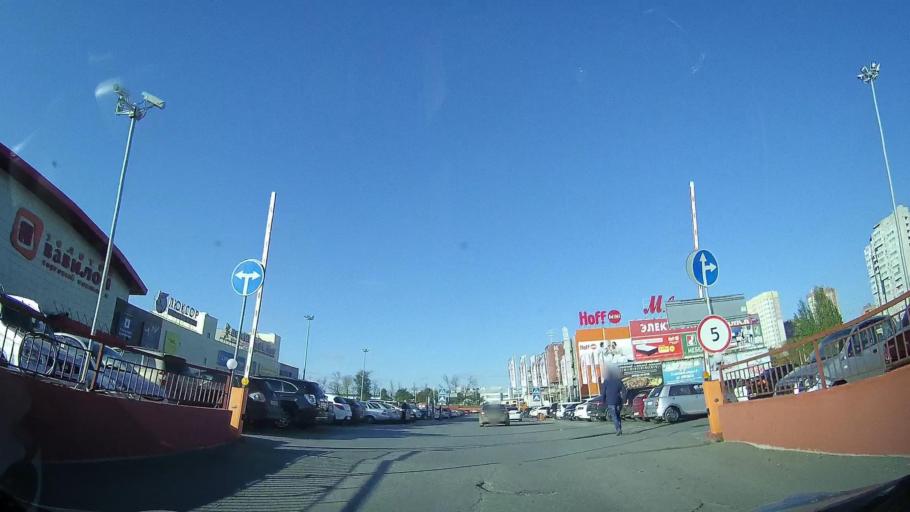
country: RU
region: Rostov
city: Kalinin
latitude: 47.2300
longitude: 39.6121
